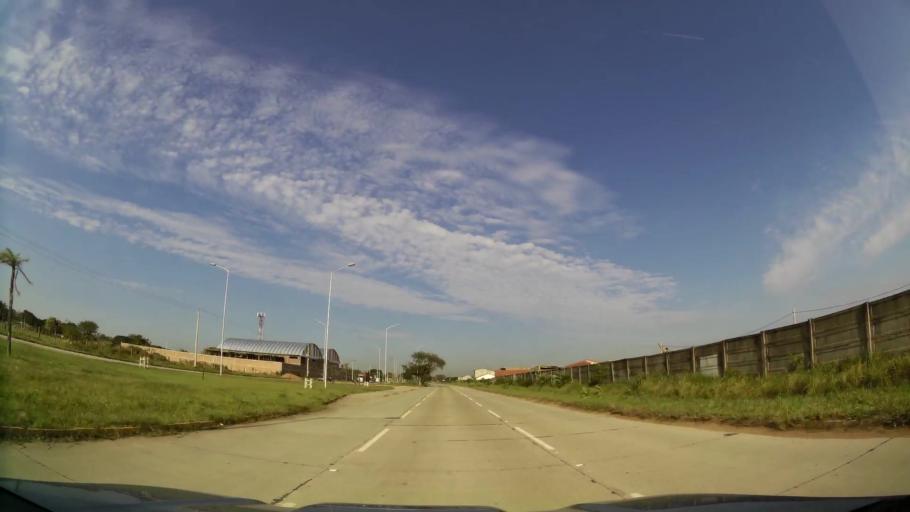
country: BO
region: Santa Cruz
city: Santa Cruz de la Sierra
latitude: -17.6988
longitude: -63.1257
